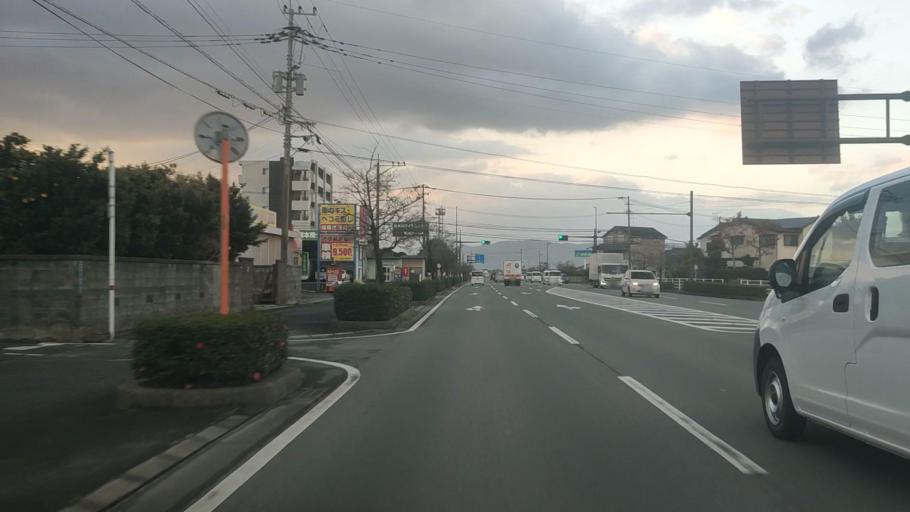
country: JP
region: Kumamoto
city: Kumamoto
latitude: 32.7603
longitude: 130.7057
